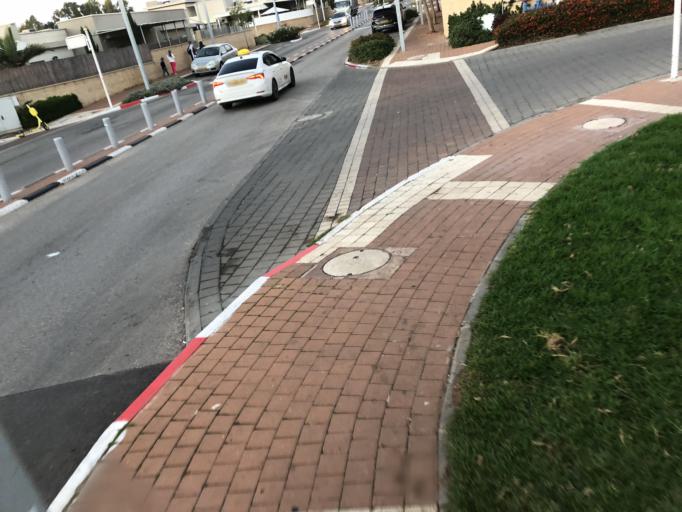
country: IL
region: Northern District
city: `Akko
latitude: 32.9344
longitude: 35.0898
